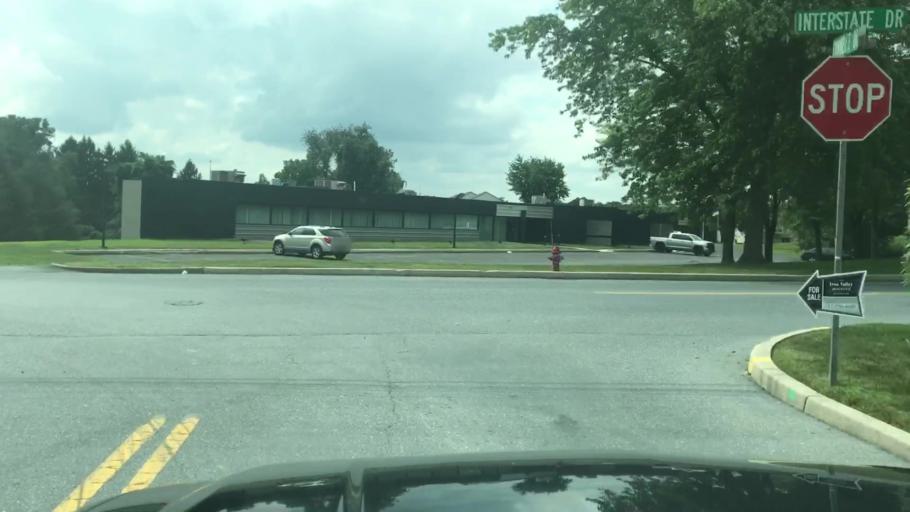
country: US
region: Pennsylvania
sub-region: Dauphin County
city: Progress
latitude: 40.3109
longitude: -76.8440
